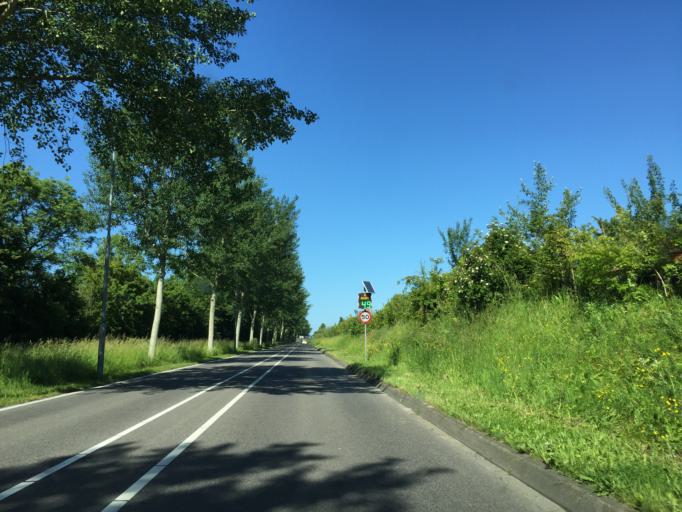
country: NL
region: Zeeland
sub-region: Gemeente Middelburg
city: Middelburg
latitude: 51.5126
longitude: 3.6099
